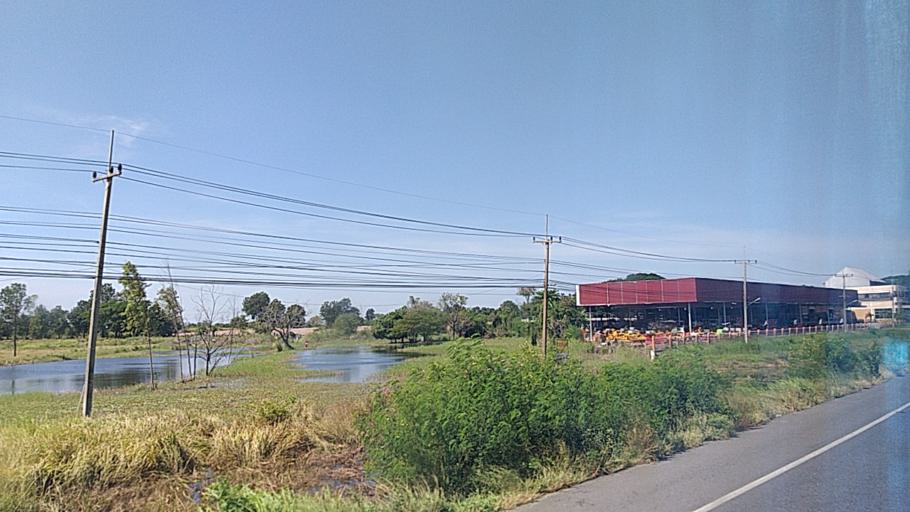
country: TH
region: Khon Kaen
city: Ban Haet
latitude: 16.2908
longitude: 102.7864
